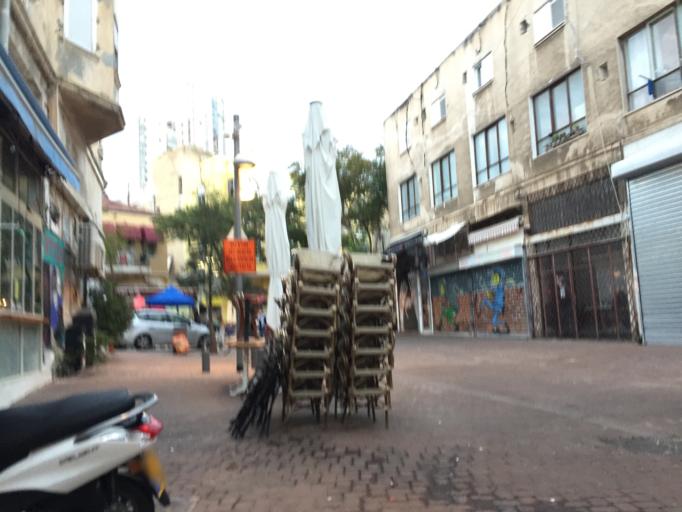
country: IL
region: Tel Aviv
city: Tel Aviv
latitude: 32.0684
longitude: 34.7698
